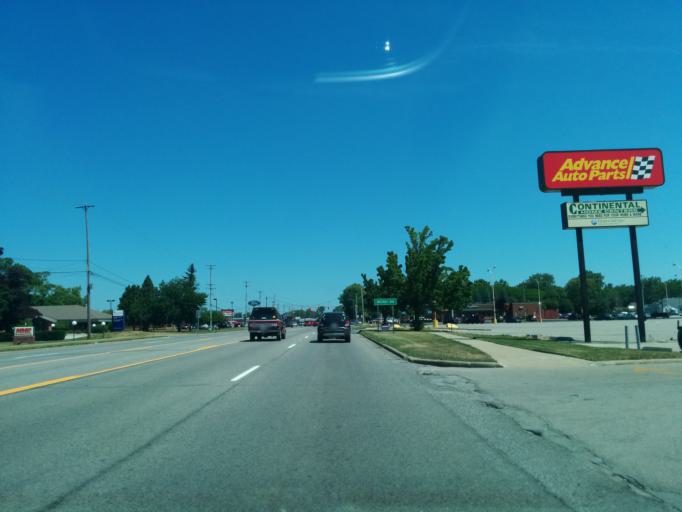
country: US
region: Michigan
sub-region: Bay County
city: Bay City
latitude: 43.6218
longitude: -83.9143
